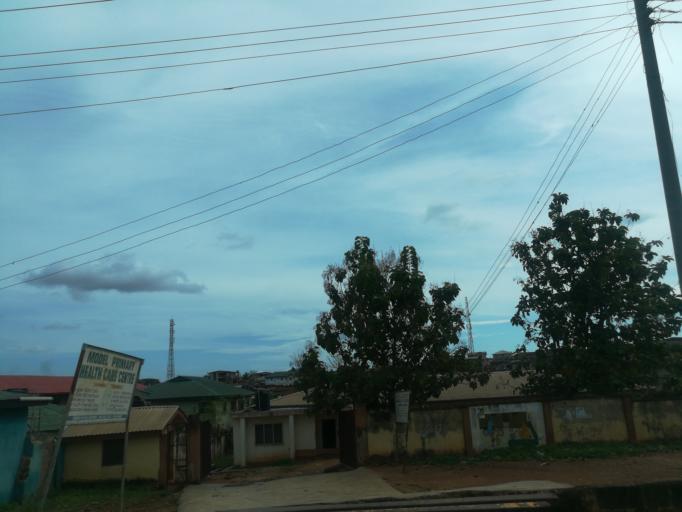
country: NG
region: Oyo
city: Ibadan
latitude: 7.3778
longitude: 3.9527
